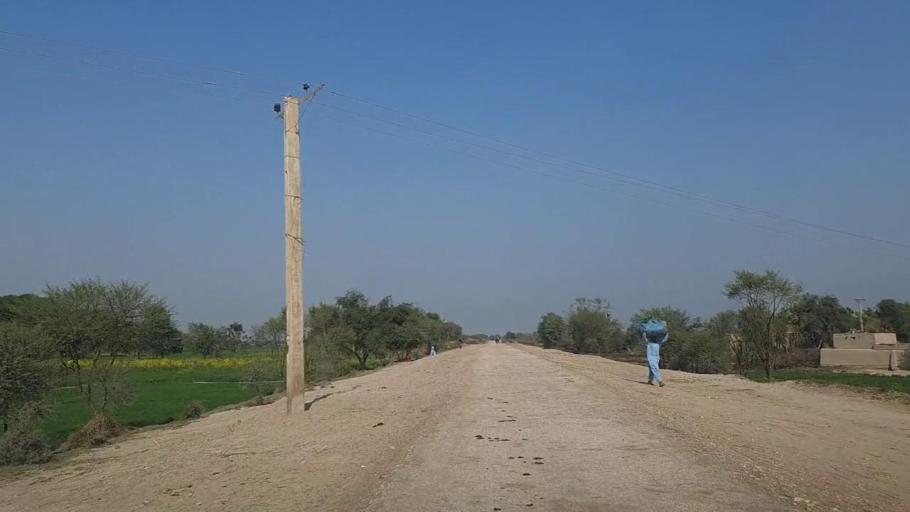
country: PK
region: Sindh
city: Moro
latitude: 26.7898
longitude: 67.9345
